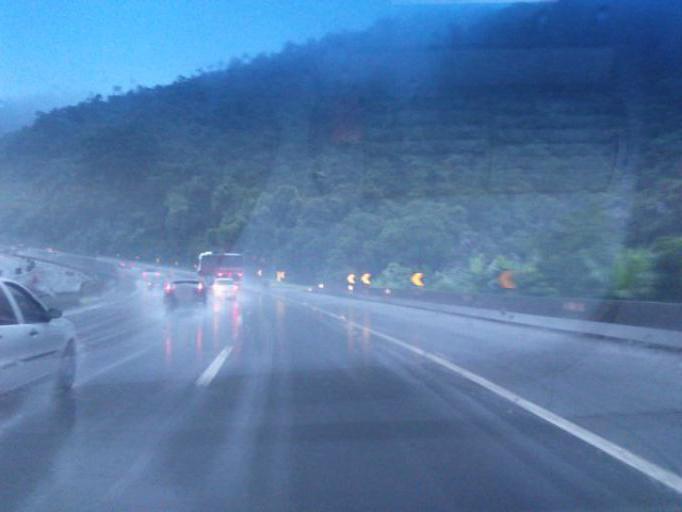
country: BR
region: Sao Paulo
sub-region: Juquitiba
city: Juquitiba
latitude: -24.0519
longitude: -47.2021
